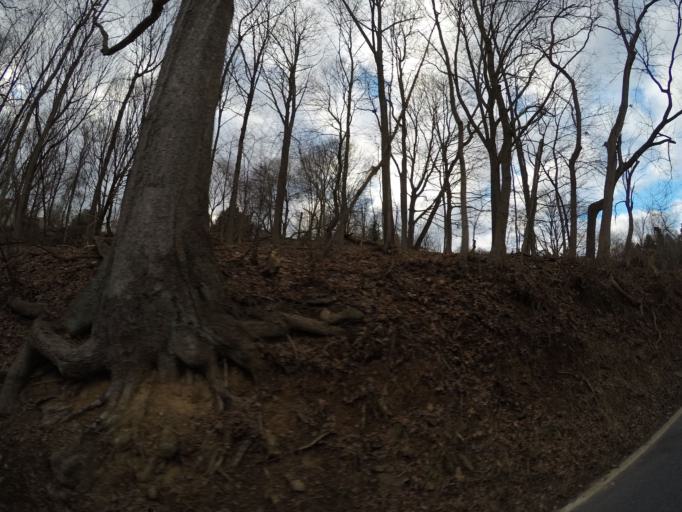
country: US
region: Maryland
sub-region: Carroll County
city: Sykesville
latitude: 39.3706
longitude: -76.9710
